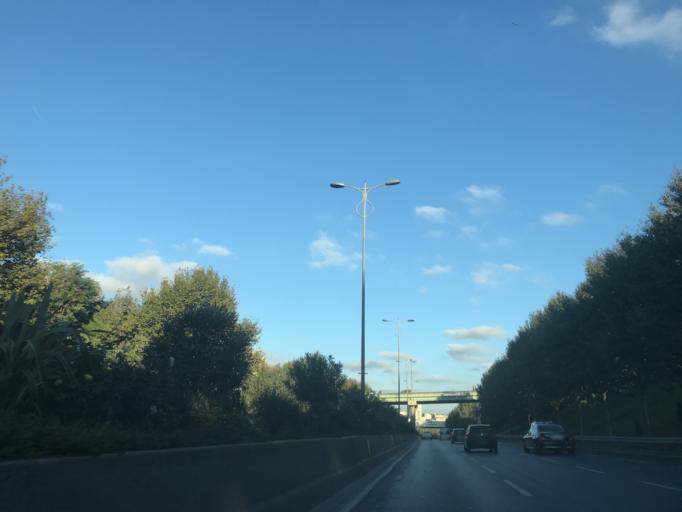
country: TR
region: Istanbul
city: Bagcilar
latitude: 41.0547
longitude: 28.8562
